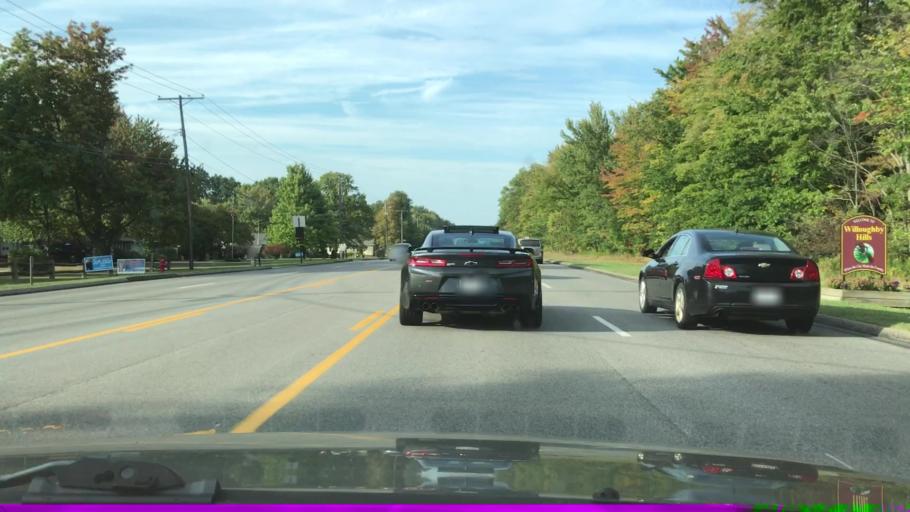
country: US
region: Ohio
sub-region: Cuyahoga County
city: Mayfield
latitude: 41.5708
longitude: -81.4393
